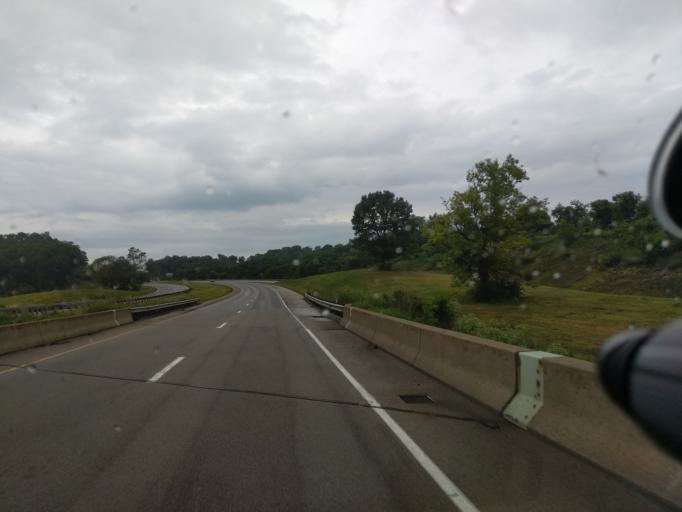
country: US
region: Pennsylvania
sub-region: Northumberland County
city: Milton
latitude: 41.0199
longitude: -76.7917
